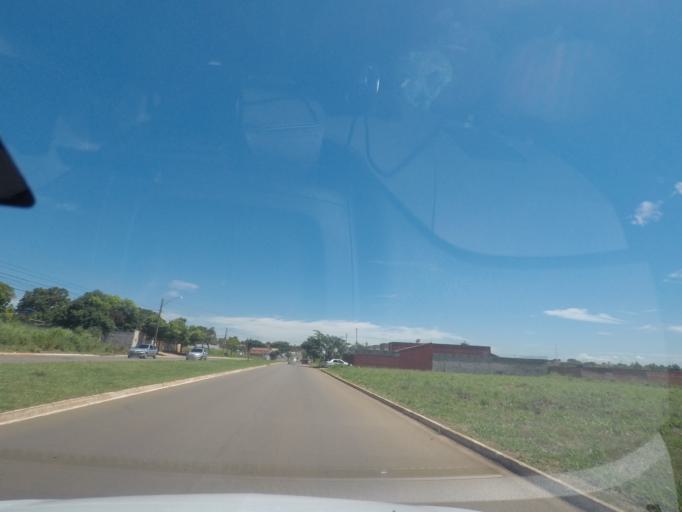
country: BR
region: Goias
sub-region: Aparecida De Goiania
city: Aparecida de Goiania
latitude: -16.7791
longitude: -49.3274
